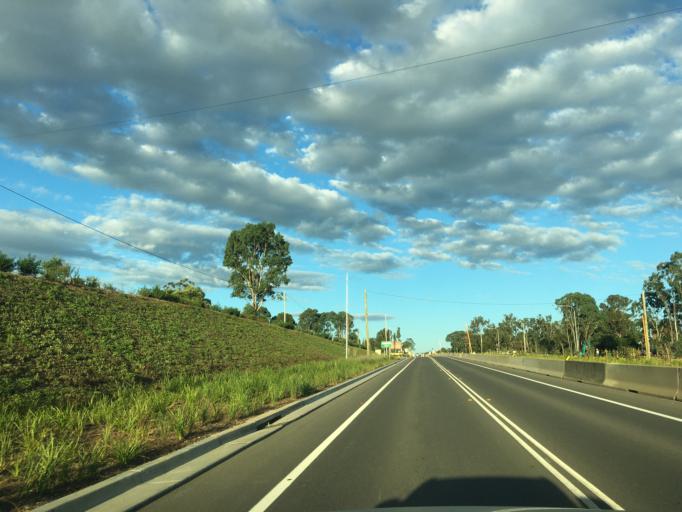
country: AU
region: New South Wales
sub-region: Liverpool
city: Bringelly
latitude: -33.9443
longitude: 150.7614
